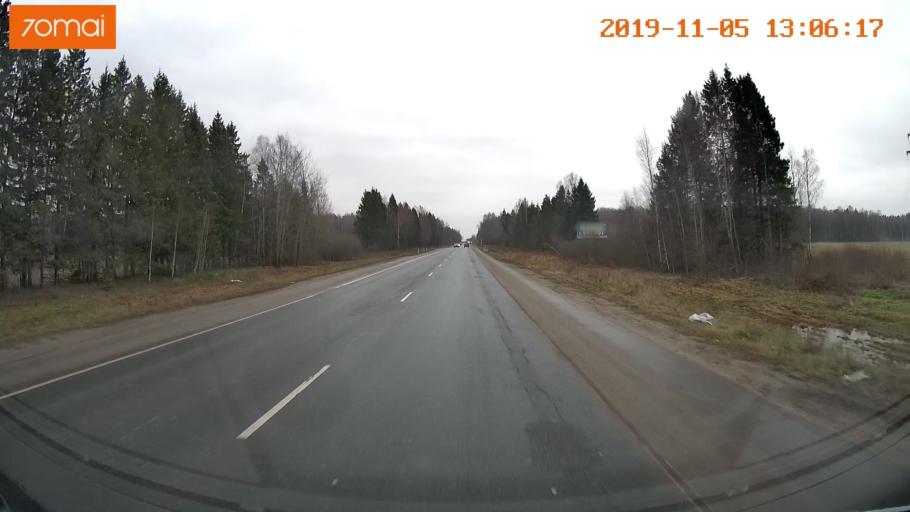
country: RU
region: Ivanovo
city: Kitovo
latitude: 56.8766
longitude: 41.2607
